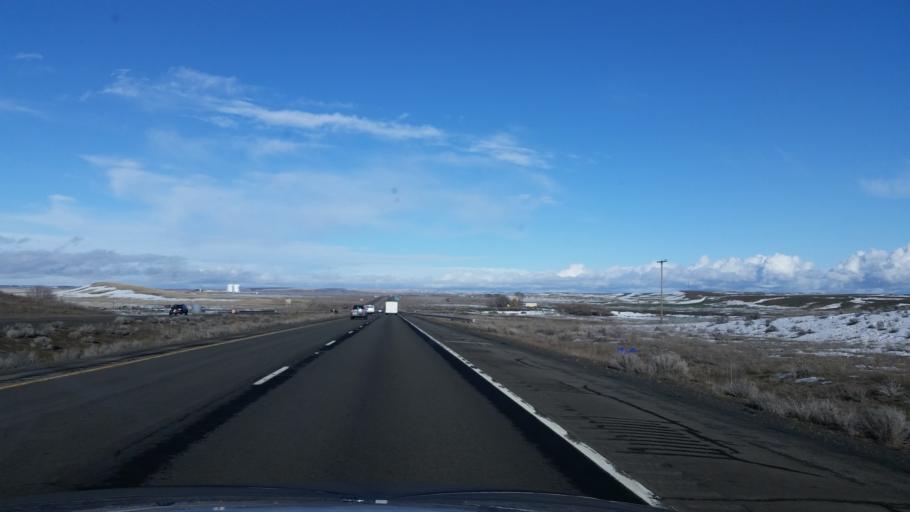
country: US
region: Washington
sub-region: Adams County
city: Ritzville
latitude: 47.1893
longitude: -118.2610
